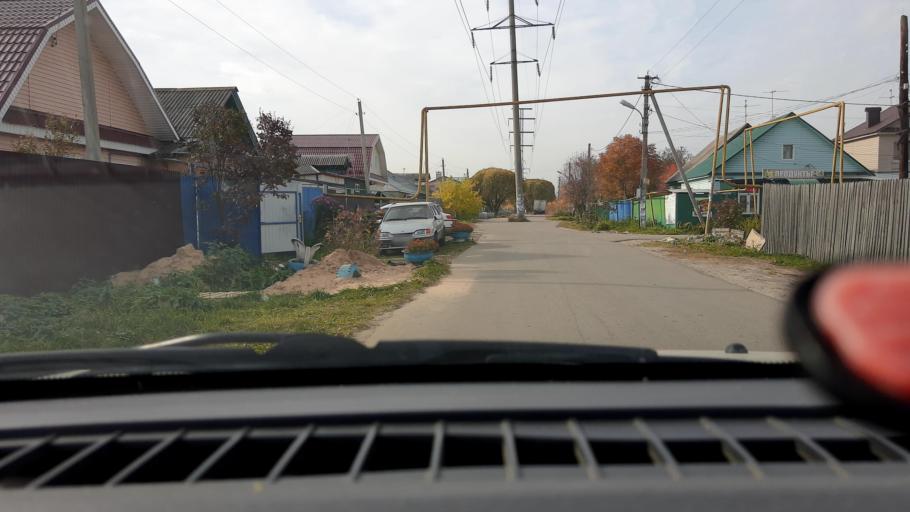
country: RU
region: Nizjnij Novgorod
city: Nizhniy Novgorod
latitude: 56.2924
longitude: 43.8968
